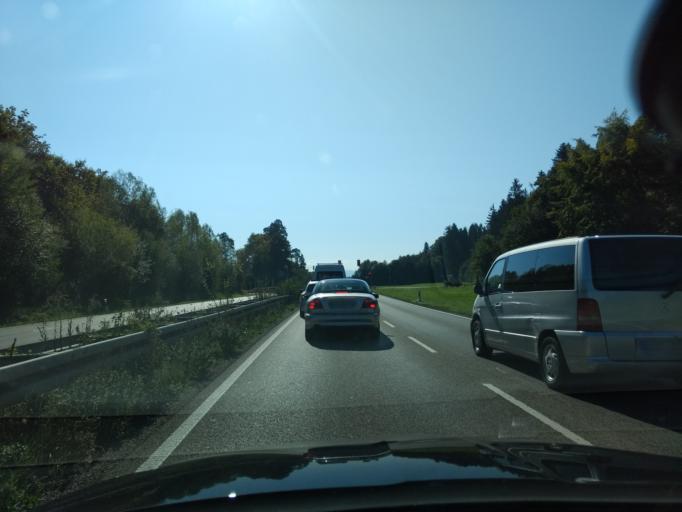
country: DE
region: Bavaria
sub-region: Upper Bavaria
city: Geretsried
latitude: 47.8835
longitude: 11.4568
